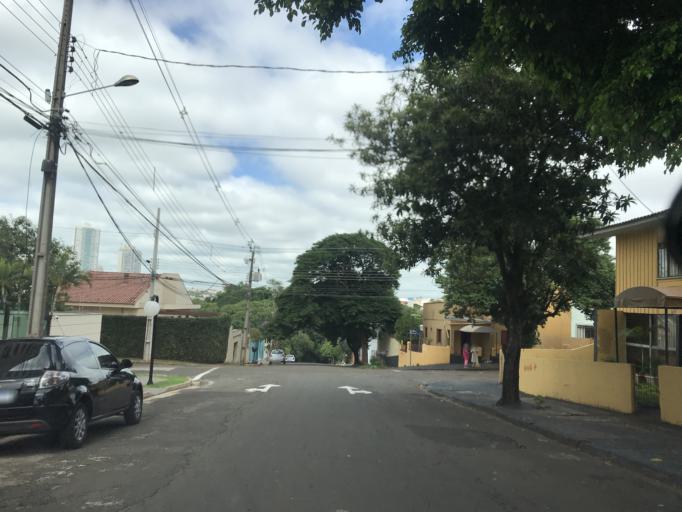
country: BR
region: Parana
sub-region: Londrina
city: Londrina
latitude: -23.3231
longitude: -51.1702
